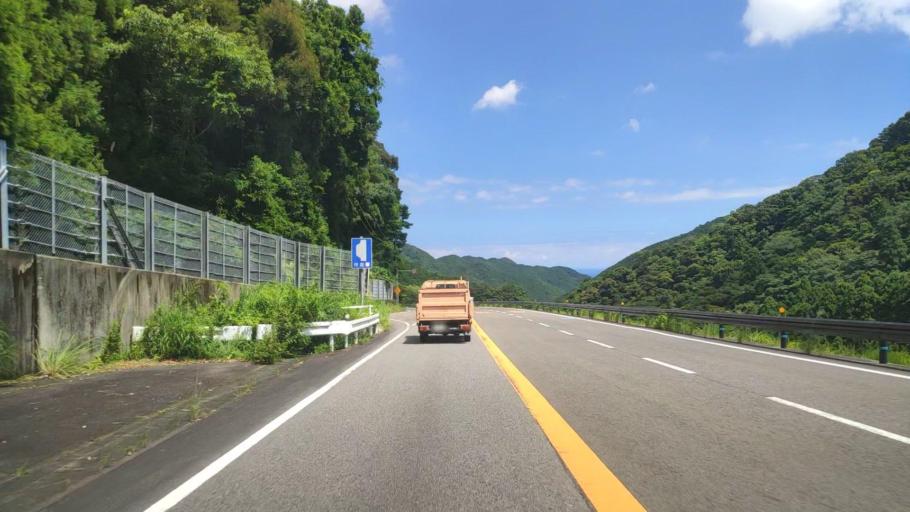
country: JP
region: Mie
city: Owase
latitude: 33.9216
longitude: 136.0972
